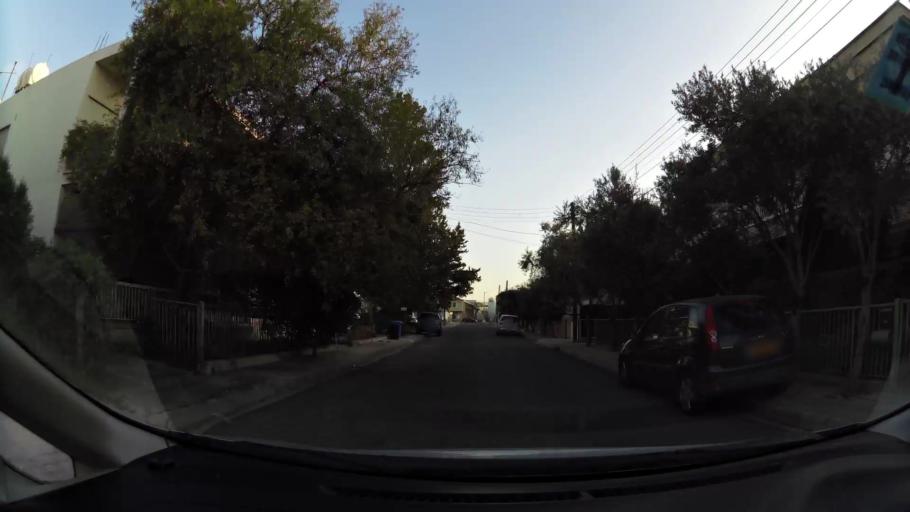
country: CY
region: Lefkosia
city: Nicosia
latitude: 35.1699
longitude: 33.3238
